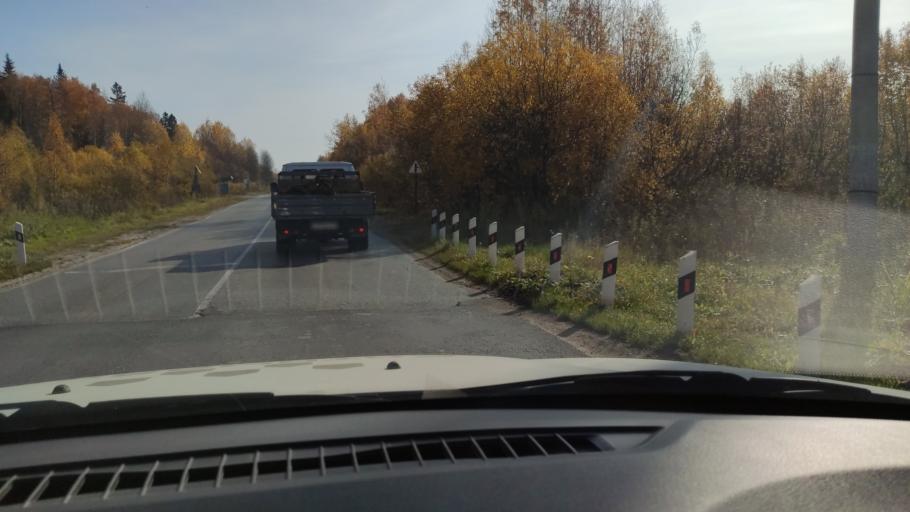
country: RU
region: Perm
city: Novyye Lyady
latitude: 58.0272
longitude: 56.6289
